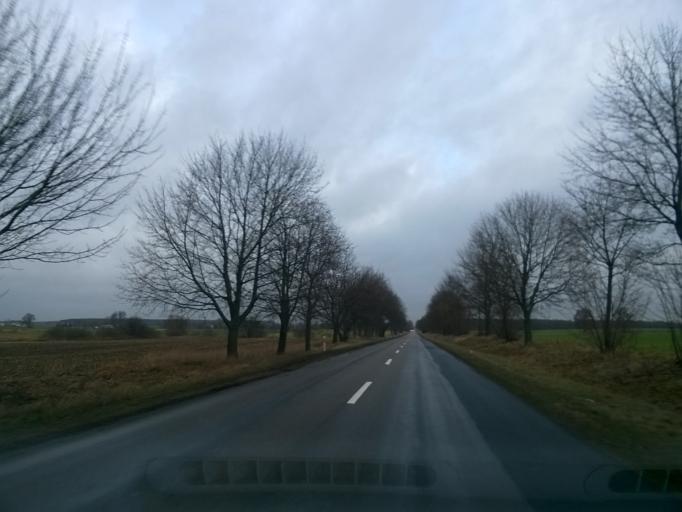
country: PL
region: Greater Poland Voivodeship
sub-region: Powiat wagrowiecki
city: Golancz
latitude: 52.9058
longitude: 17.3598
